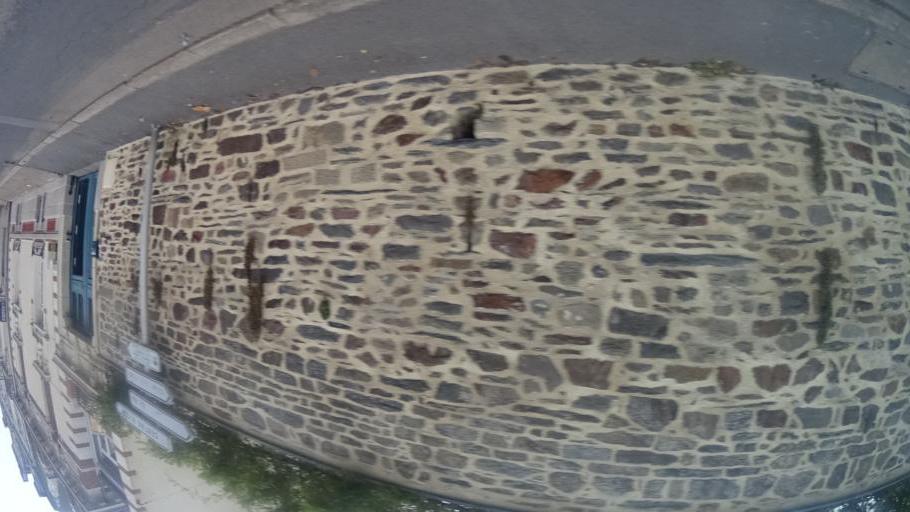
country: FR
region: Brittany
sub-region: Departement d'Ille-et-Vilaine
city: Redon
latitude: 47.6524
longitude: -2.0881
